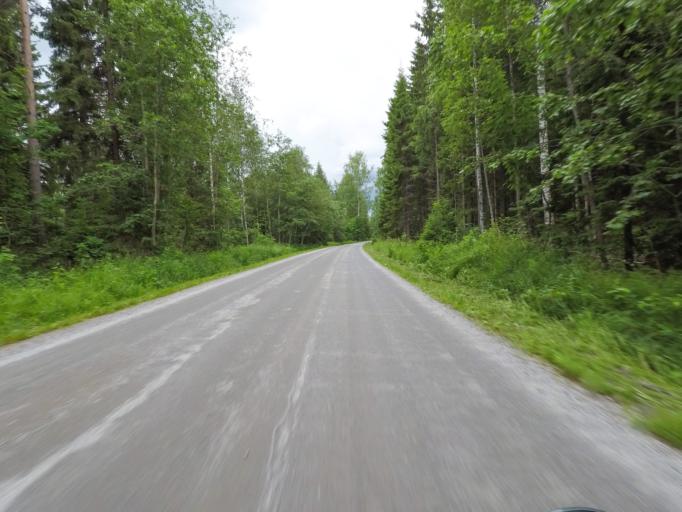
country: FI
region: Central Finland
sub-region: Jyvaeskylae
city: Hankasalmi
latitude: 62.4204
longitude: 26.6456
